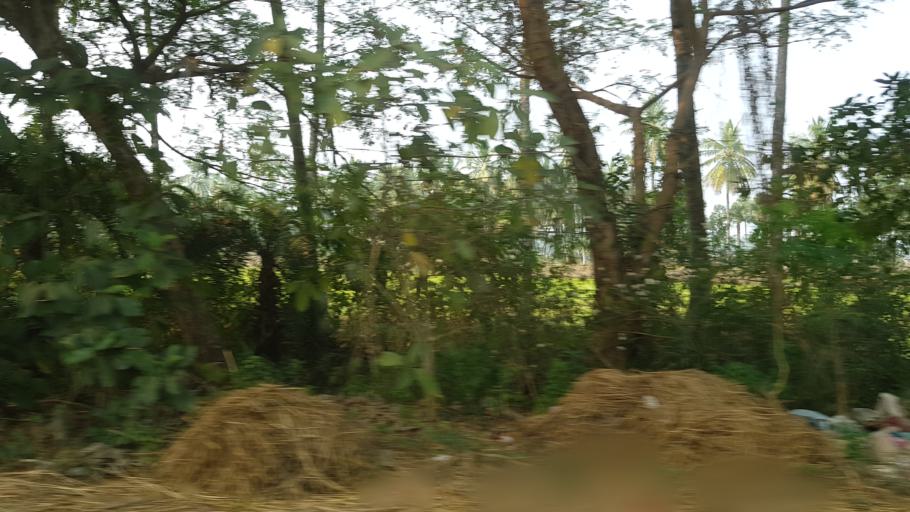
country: IN
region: Andhra Pradesh
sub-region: West Godavari
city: Akividu
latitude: 16.5341
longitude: 81.3967
